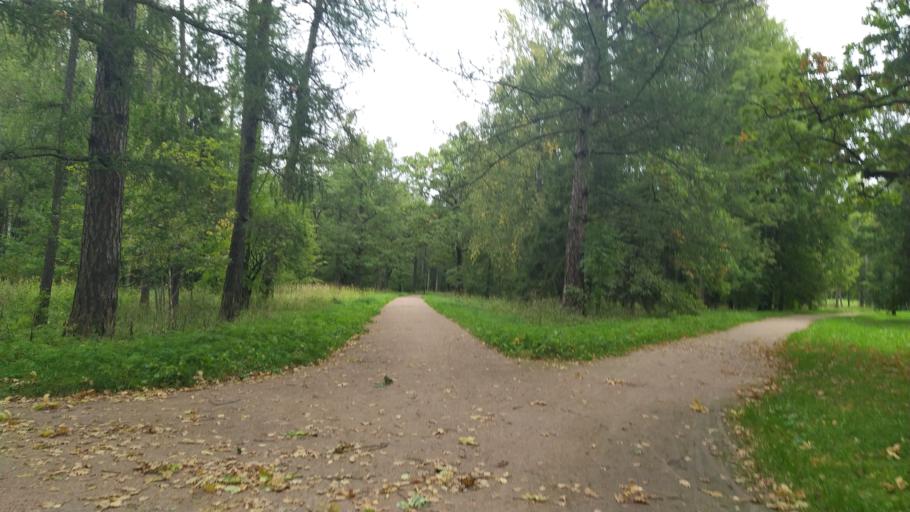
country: RU
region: St.-Petersburg
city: Pushkin
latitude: 59.7206
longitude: 30.3834
